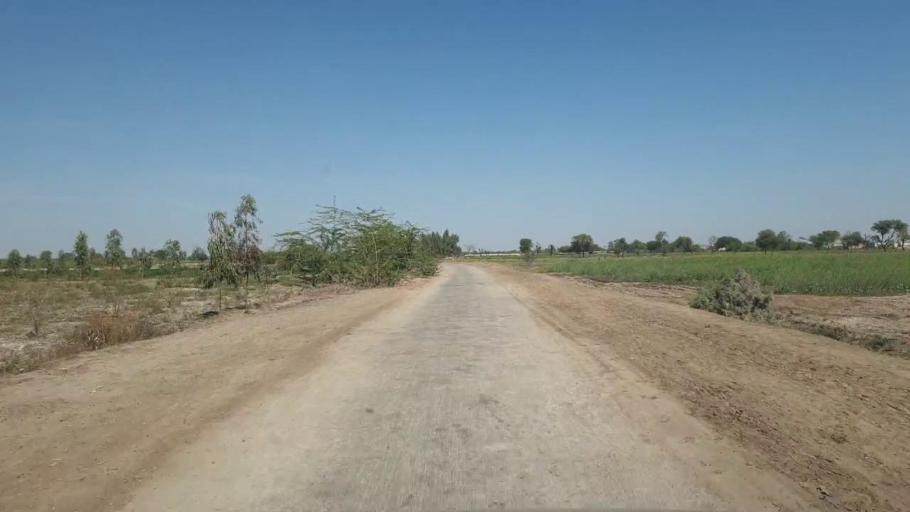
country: PK
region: Sindh
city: Dhoro Naro
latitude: 25.4651
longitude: 69.6059
